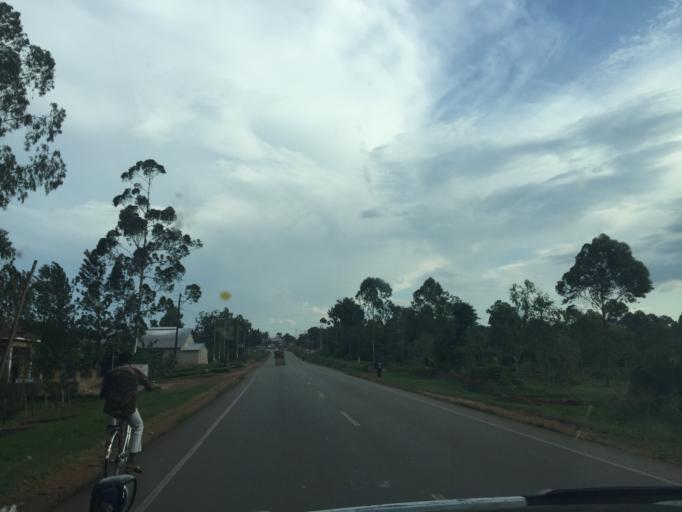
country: UG
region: Central Region
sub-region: Luwero District
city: Luwero
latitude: 0.8557
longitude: 32.4865
